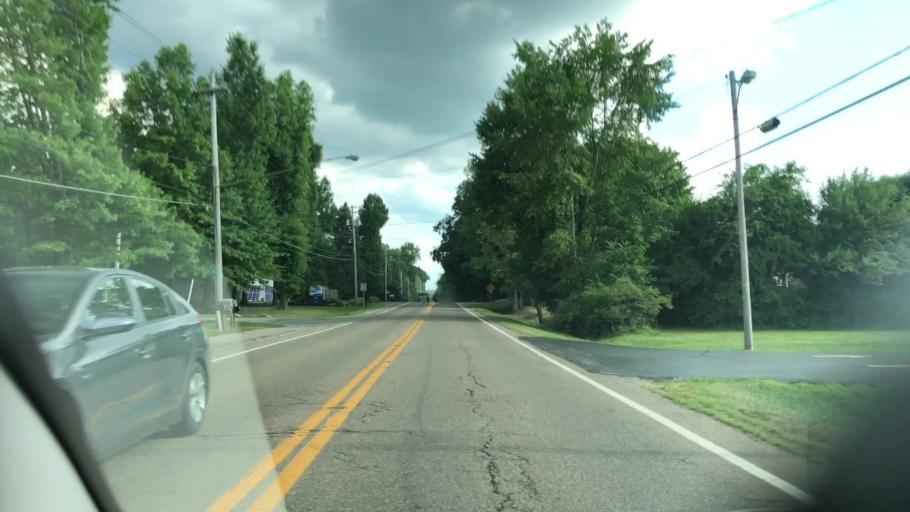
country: US
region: Ohio
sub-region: Summit County
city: Fairlawn
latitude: 41.0914
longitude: -81.6446
